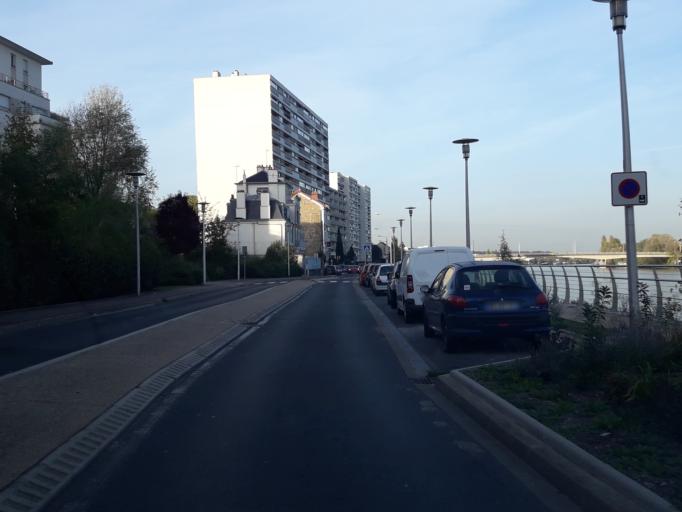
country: FR
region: Ile-de-France
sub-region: Departement de l'Essonne
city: Juvisy-sur-Orge
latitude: 48.6851
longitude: 2.3852
